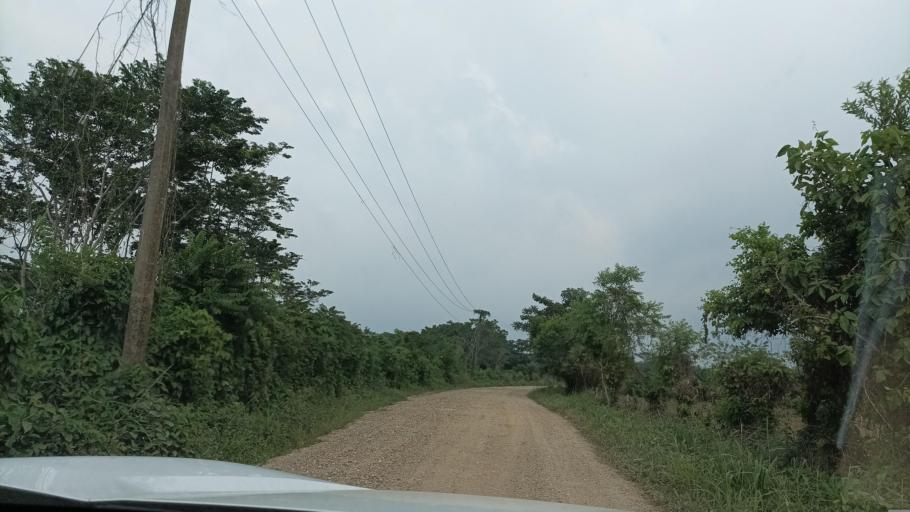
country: MX
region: Veracruz
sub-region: Moloacan
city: Cuichapa
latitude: 17.5837
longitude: -94.2080
